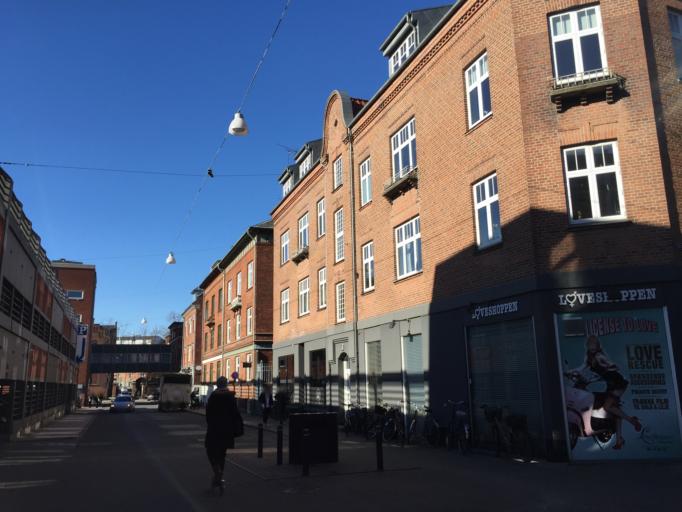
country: DK
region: South Denmark
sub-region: Odense Kommune
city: Odense
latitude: 55.3962
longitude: 10.3847
